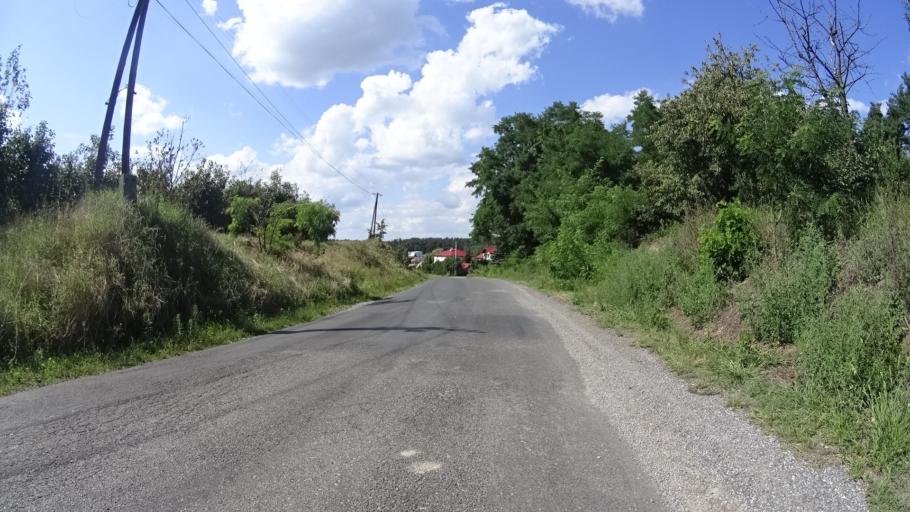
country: PL
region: Masovian Voivodeship
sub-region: Powiat grojecki
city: Mogielnica
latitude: 51.6897
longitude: 20.7488
